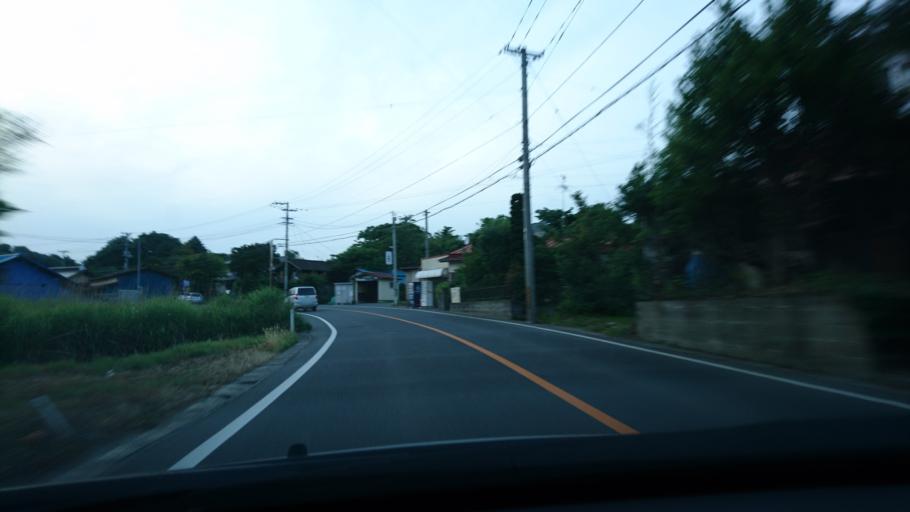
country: JP
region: Miyagi
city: Furukawa
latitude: 38.7522
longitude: 141.0128
